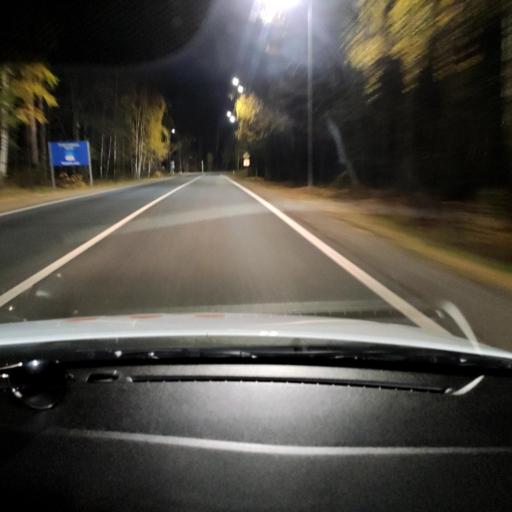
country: RU
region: Tatarstan
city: Verkhniy Uslon
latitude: 55.6387
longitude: 49.0227
